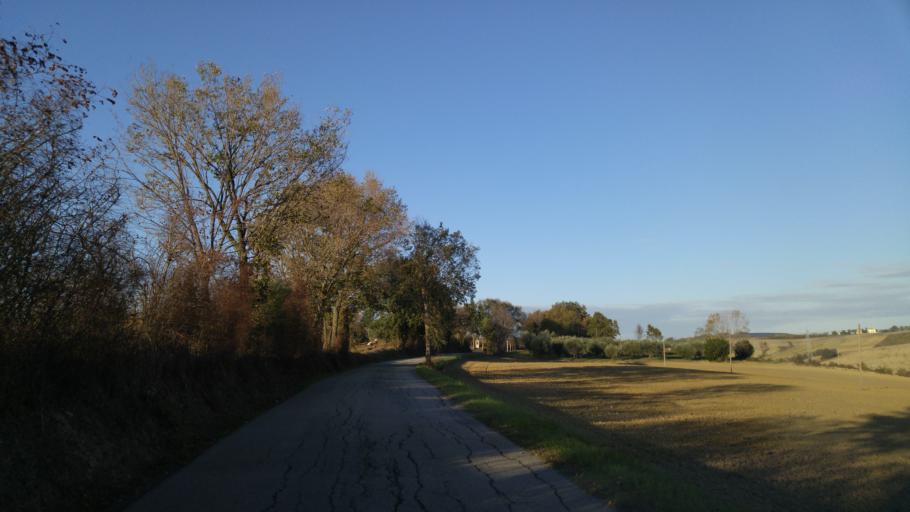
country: IT
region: The Marches
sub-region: Provincia di Pesaro e Urbino
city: Cartoceto
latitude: 43.7924
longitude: 12.8993
